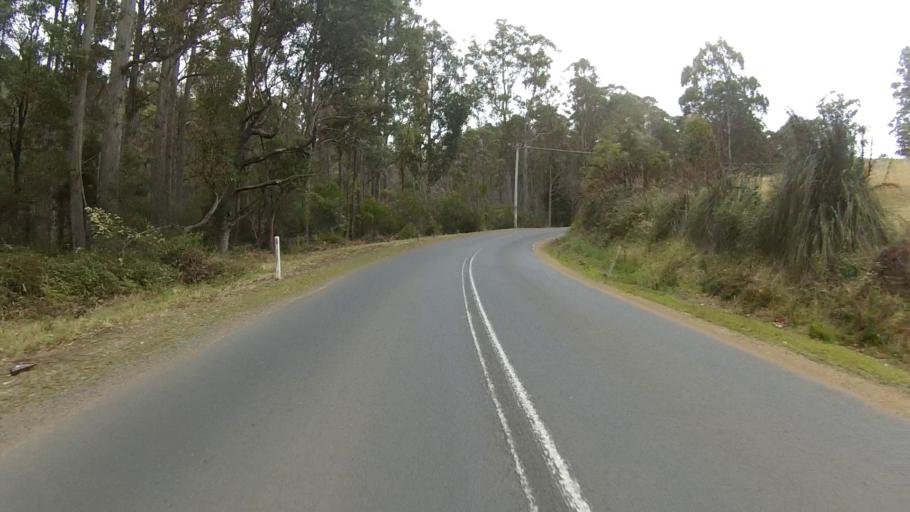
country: AU
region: Tasmania
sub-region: Huon Valley
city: Cygnet
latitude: -43.1398
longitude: 147.1522
